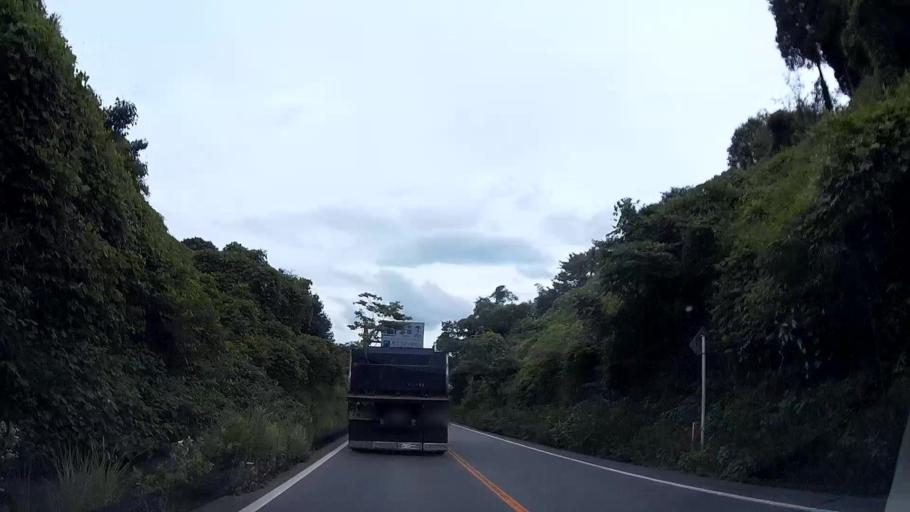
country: JP
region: Oita
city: Tsukawaki
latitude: 33.1258
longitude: 131.0610
